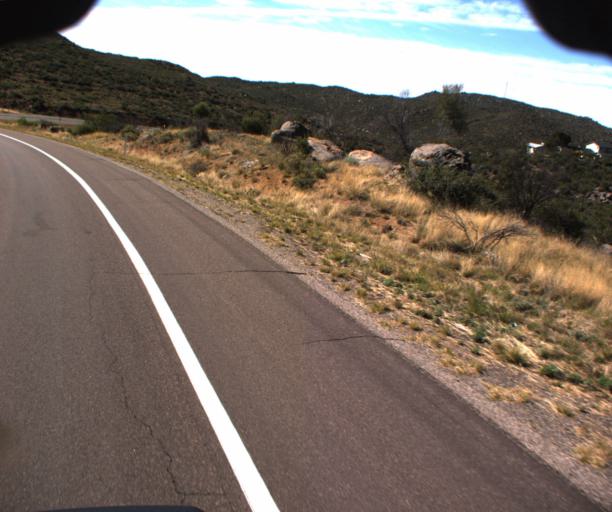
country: US
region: Arizona
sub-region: Yavapai County
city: Congress
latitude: 34.2090
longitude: -112.7550
